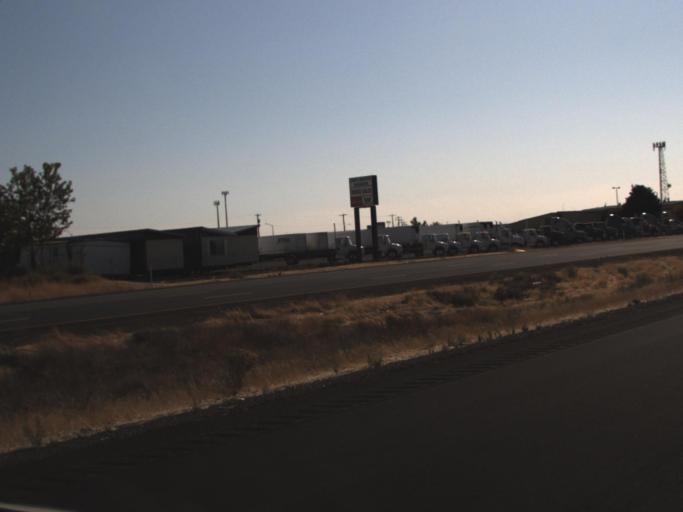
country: US
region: Washington
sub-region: Franklin County
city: Pasco
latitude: 46.2581
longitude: -119.0846
